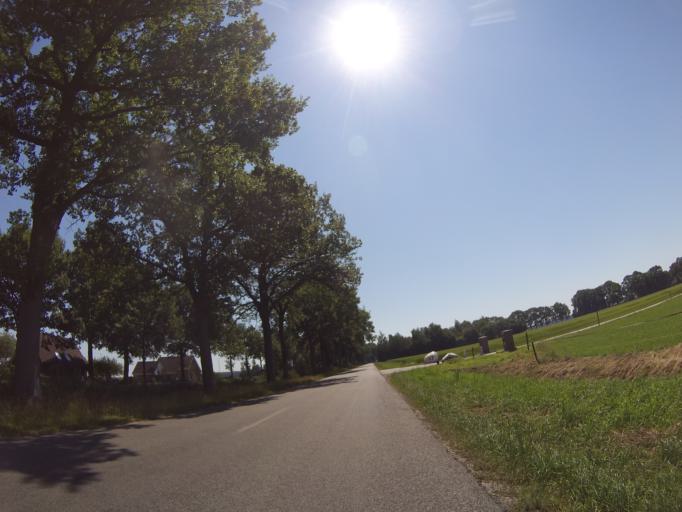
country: NL
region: Drenthe
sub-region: Gemeente Coevorden
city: Sleen
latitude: 52.8429
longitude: 6.7870
